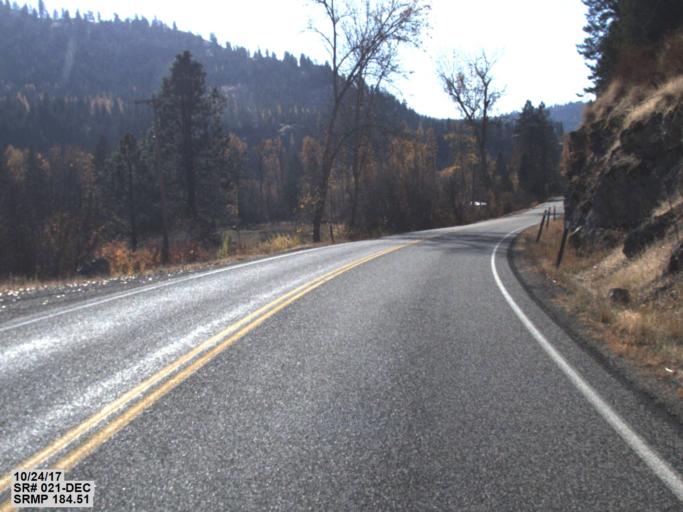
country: CA
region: British Columbia
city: Grand Forks
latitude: 48.9216
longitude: -118.5655
